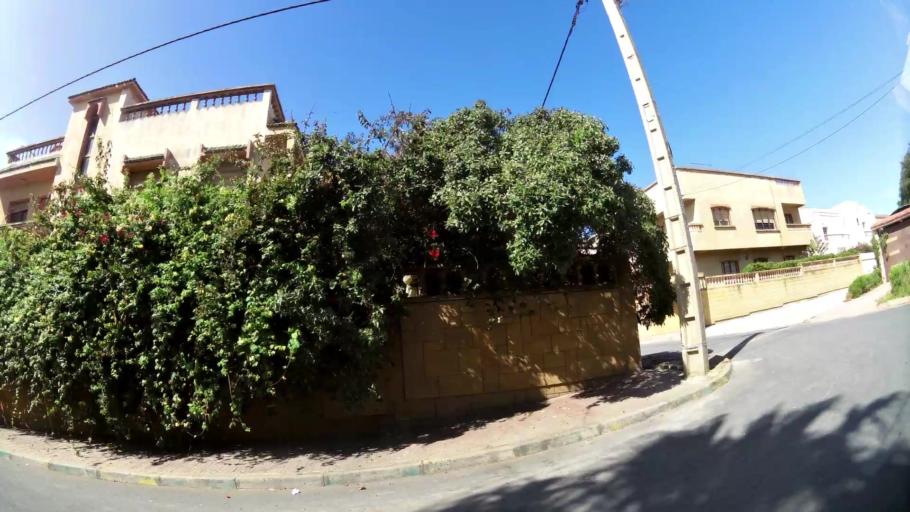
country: MA
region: Rabat-Sale-Zemmour-Zaer
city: Sale
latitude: 34.0695
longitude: -6.8033
